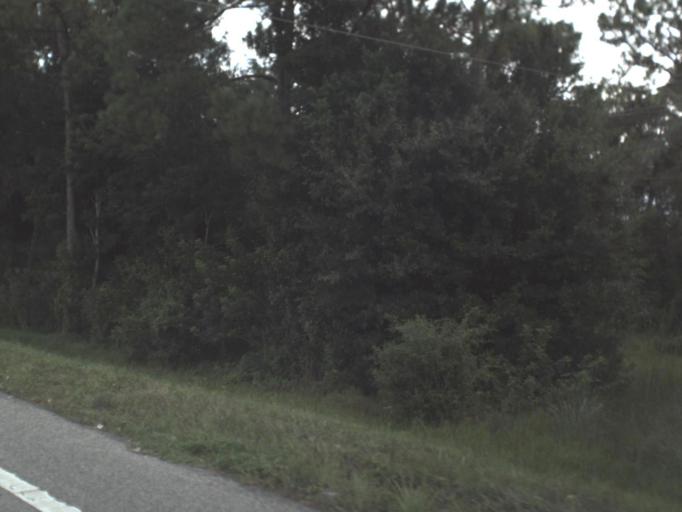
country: US
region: Florida
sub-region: Pasco County
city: Land O' Lakes
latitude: 28.3032
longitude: -82.4975
